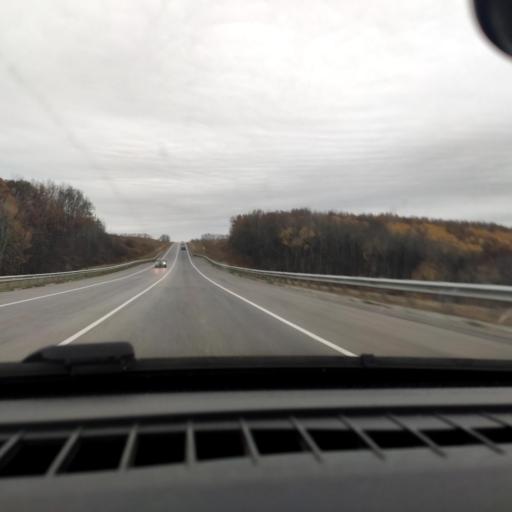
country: RU
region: Voronezj
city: Strelitsa
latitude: 51.5206
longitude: 38.9680
